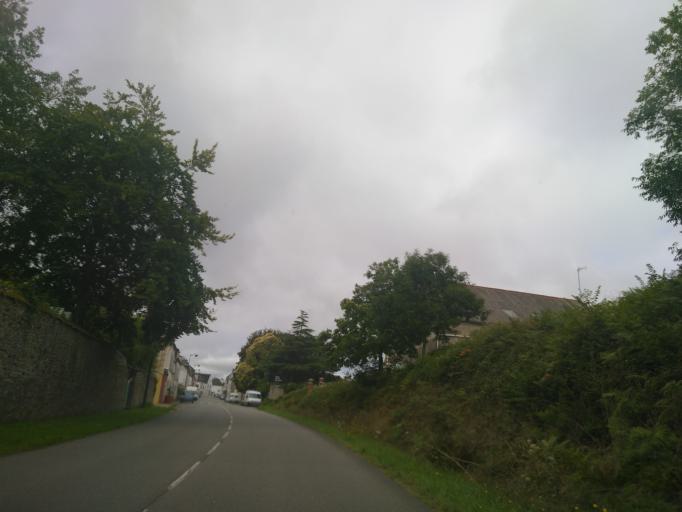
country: FR
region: Brittany
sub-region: Departement du Finistere
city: Plouhinec
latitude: 48.0439
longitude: -4.4845
